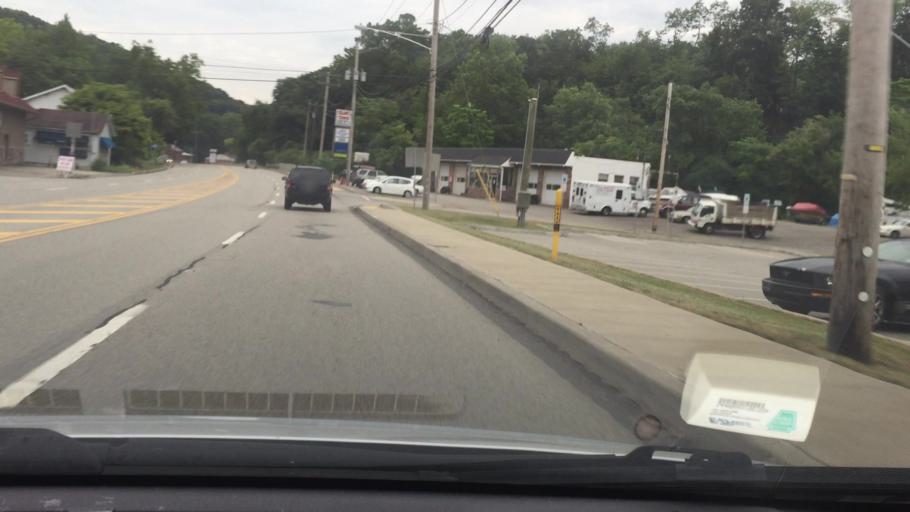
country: US
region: Pennsylvania
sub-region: Allegheny County
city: Allison Park
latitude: 40.5586
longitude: -79.9592
